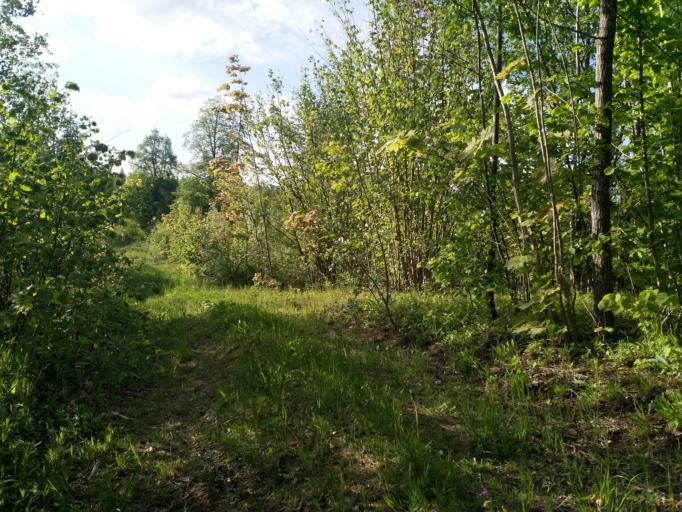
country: LV
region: Kuldigas Rajons
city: Kuldiga
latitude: 56.8574
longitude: 21.8641
